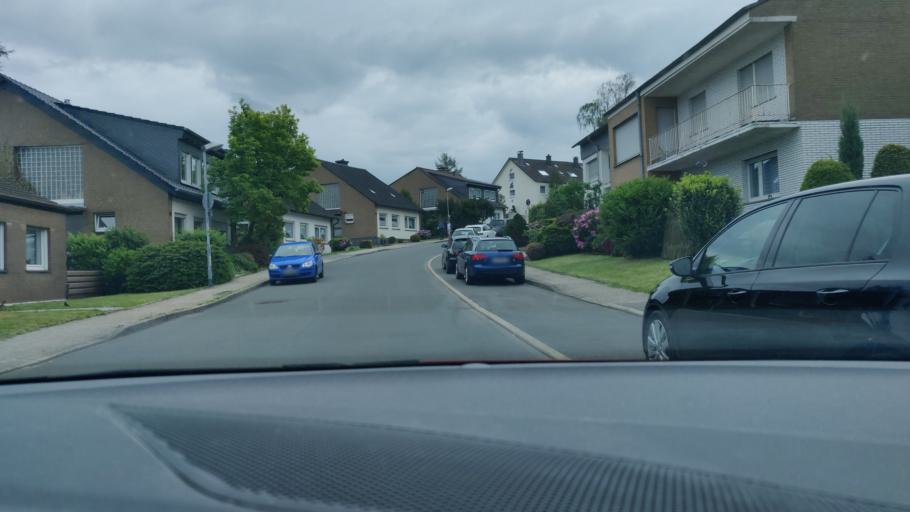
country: DE
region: North Rhine-Westphalia
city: Wulfrath
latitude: 51.3012
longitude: 7.0874
